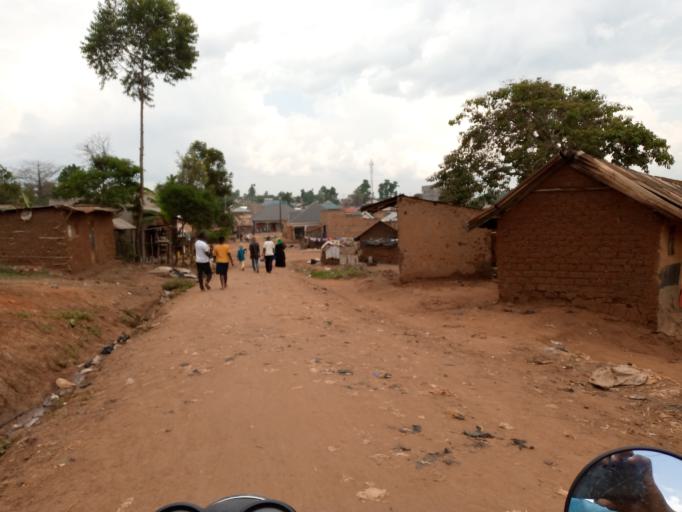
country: UG
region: Eastern Region
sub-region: Mbale District
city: Mbale
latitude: 1.0851
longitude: 34.1653
